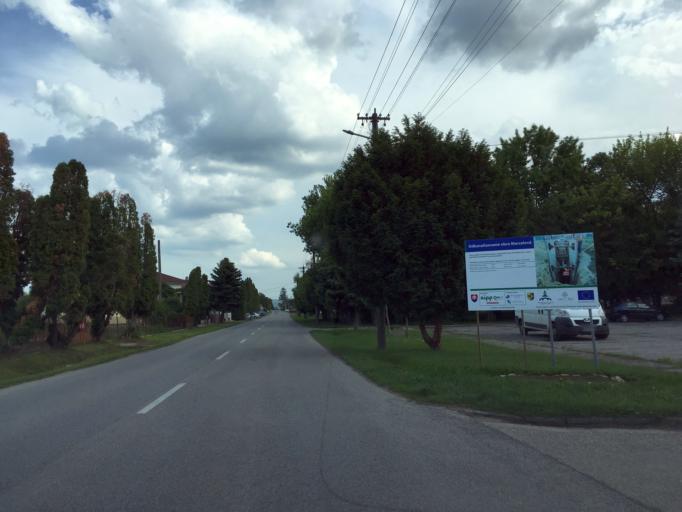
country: HU
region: Komarom-Esztergom
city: Dunaalmas
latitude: 47.7871
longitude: 18.2923
